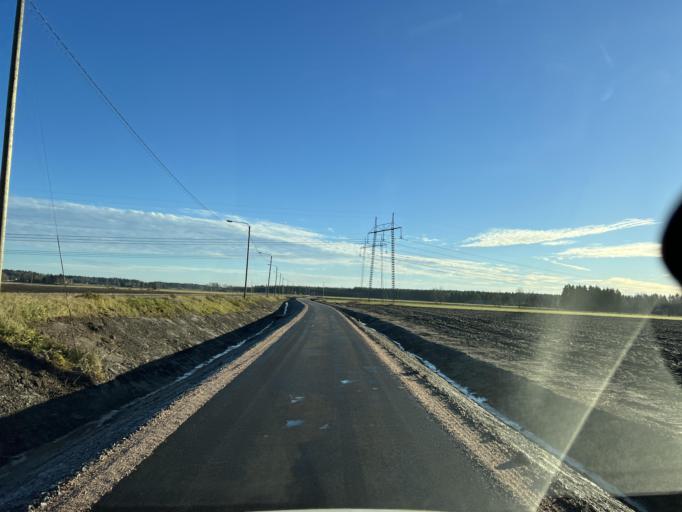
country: FI
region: Northern Ostrobothnia
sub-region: Nivala-Haapajaervi
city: Nivala
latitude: 63.9544
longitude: 24.8656
